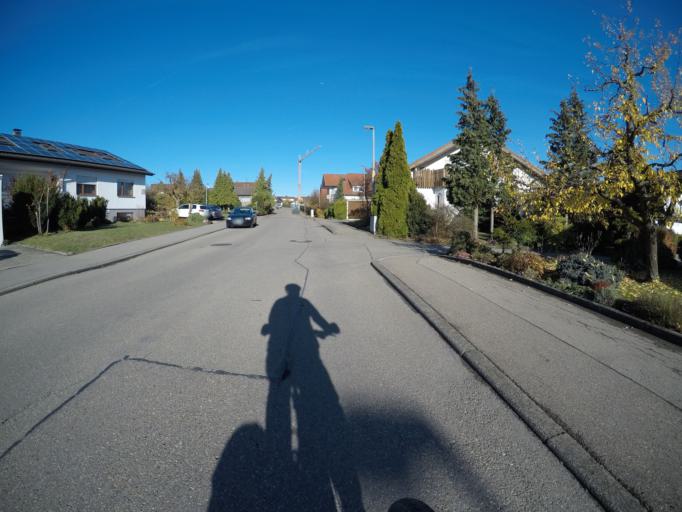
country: DE
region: Baden-Wuerttemberg
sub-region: Regierungsbezirk Stuttgart
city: Herrenberg
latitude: 48.6052
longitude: 8.8613
